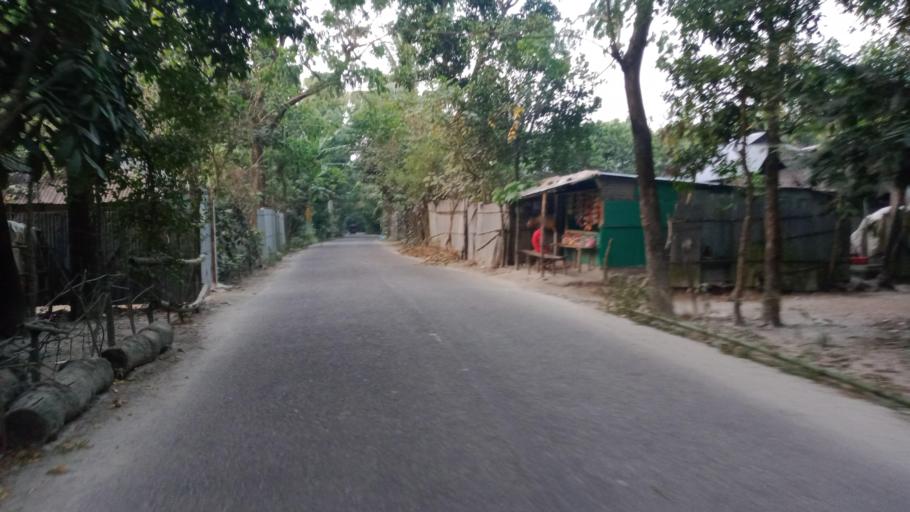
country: BD
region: Chittagong
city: Hajiganj
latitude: 23.3679
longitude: 90.9840
